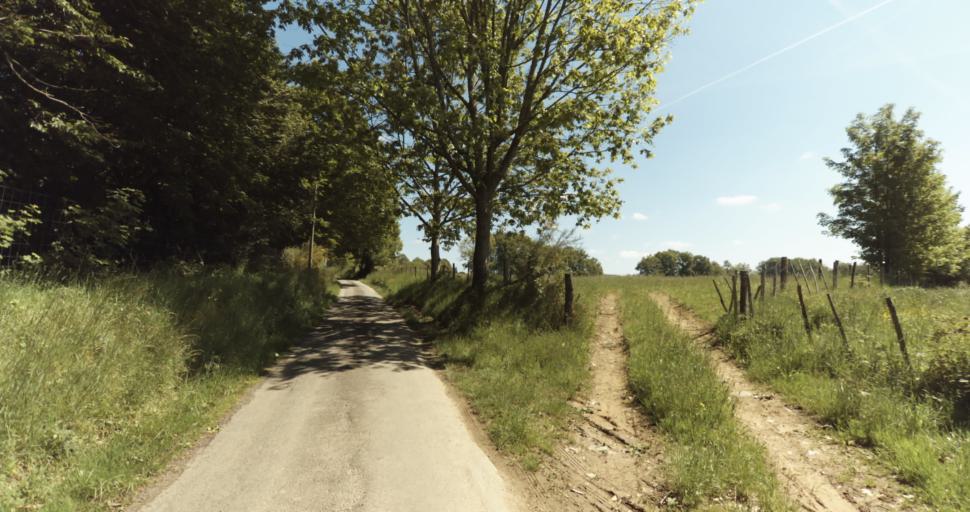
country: FR
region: Limousin
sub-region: Departement de la Haute-Vienne
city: Le Vigen
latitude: 45.7569
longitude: 1.3044
